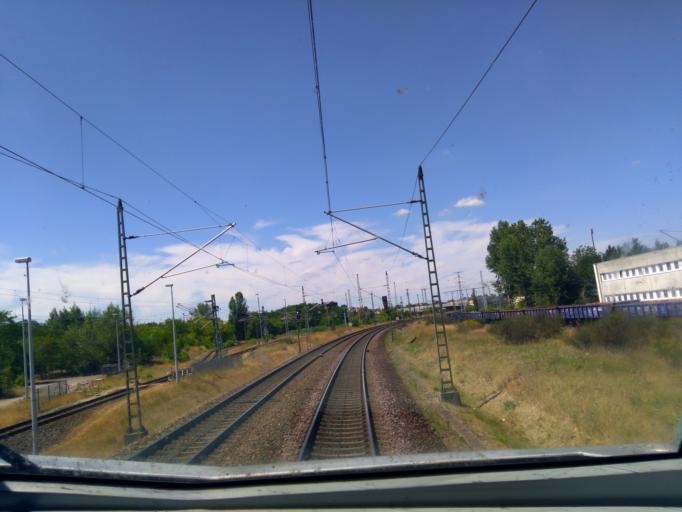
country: DE
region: Brandenburg
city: Wittenberge
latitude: 52.9947
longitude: 11.7705
